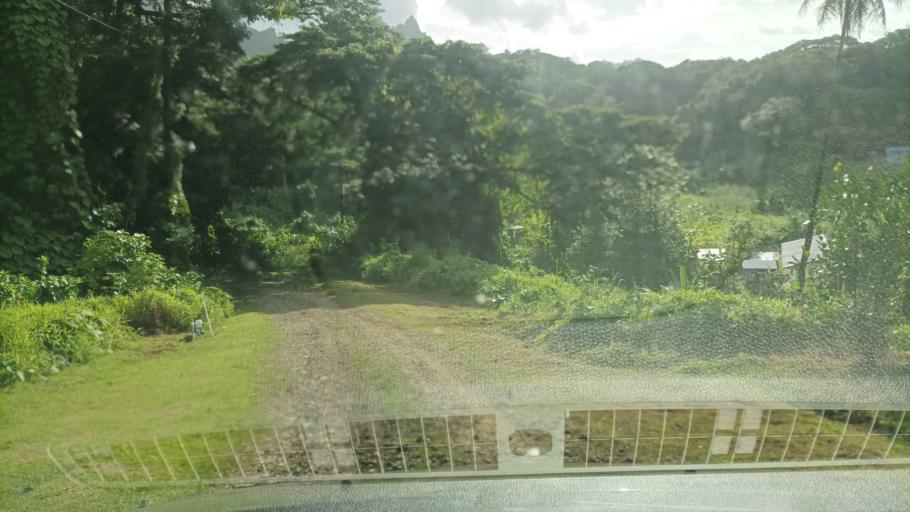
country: FM
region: Kosrae
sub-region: Lelu Municipality
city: Tofol
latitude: 5.3242
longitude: 163.0087
